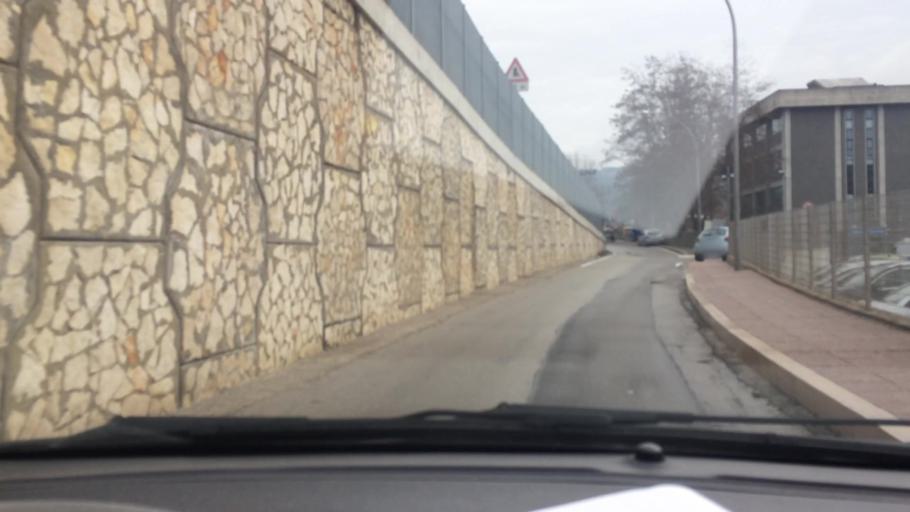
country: IT
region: Basilicate
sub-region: Provincia di Potenza
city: Potenza
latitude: 40.6285
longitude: 15.7977
